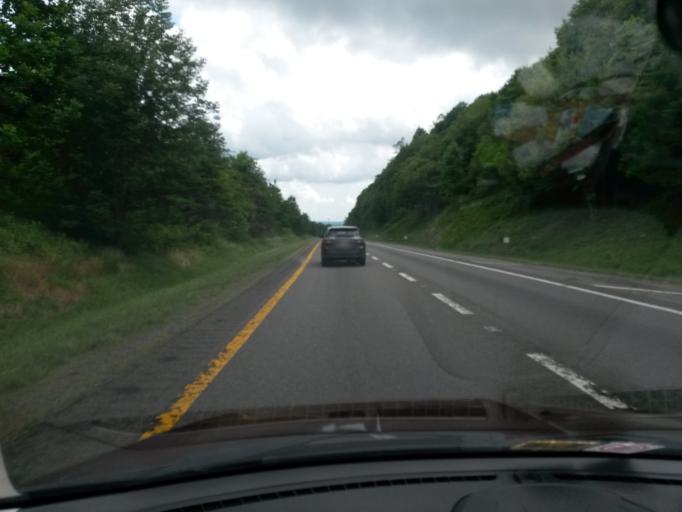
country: US
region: Virginia
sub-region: Carroll County
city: Cana
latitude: 36.5940
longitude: -80.7429
